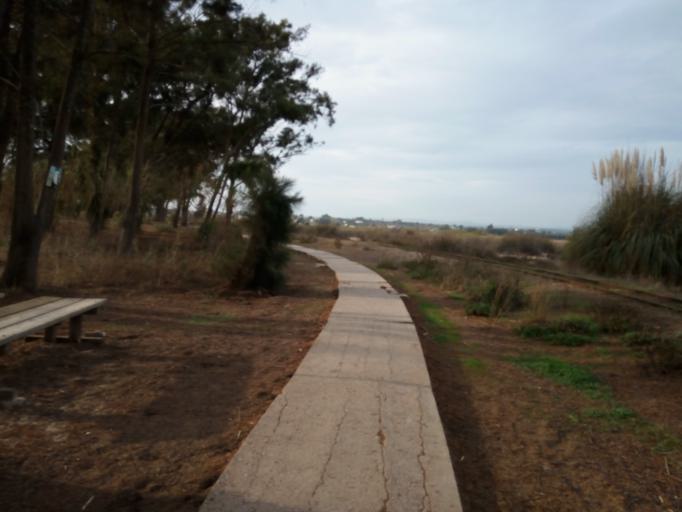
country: PT
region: Faro
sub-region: Tavira
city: Luz
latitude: 37.0881
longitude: -7.6643
